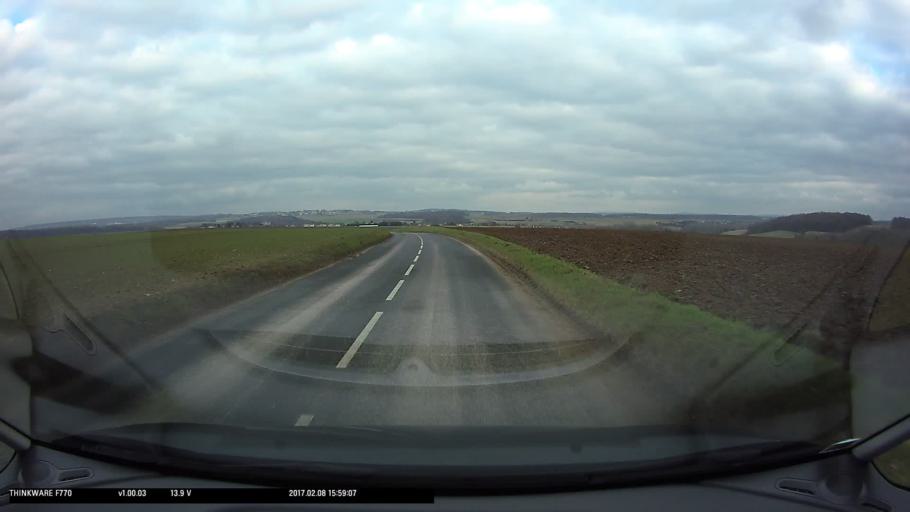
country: FR
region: Ile-de-France
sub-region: Departement du Val-d'Oise
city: Us
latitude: 49.0941
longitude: 1.9463
